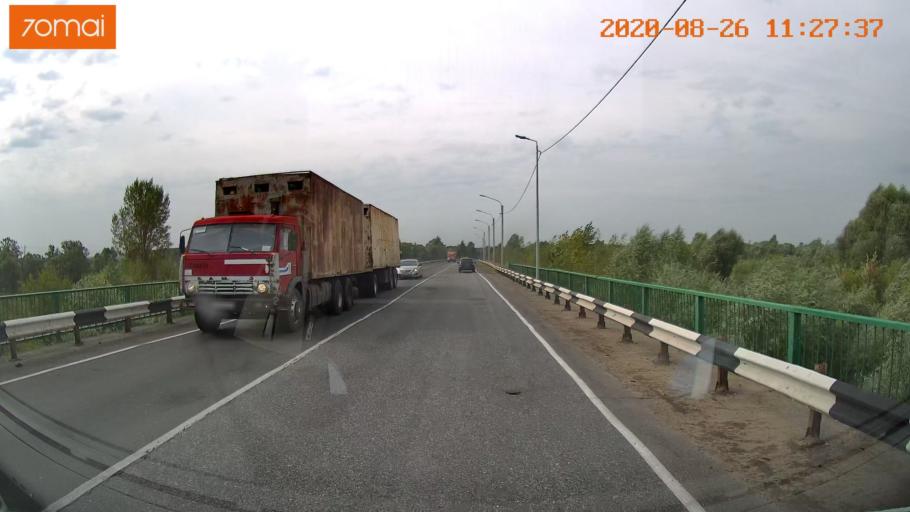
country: RU
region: Rjazan
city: Shilovo
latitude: 54.3254
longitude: 40.9304
